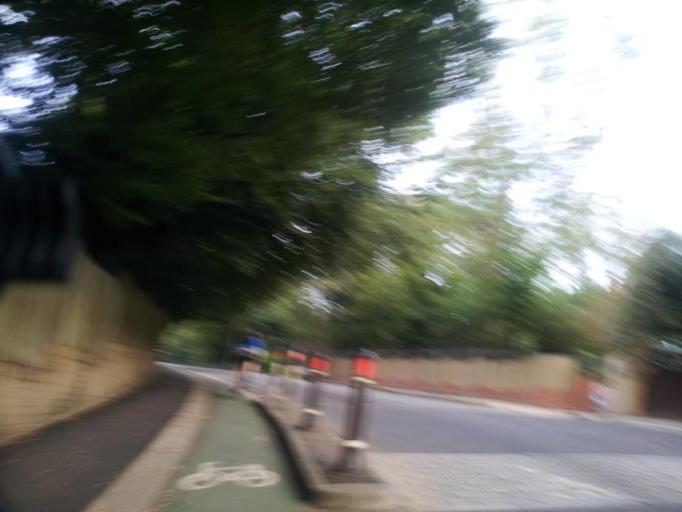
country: GB
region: England
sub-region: Greater London
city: Thornton Heath
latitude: 51.4281
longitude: -0.0771
